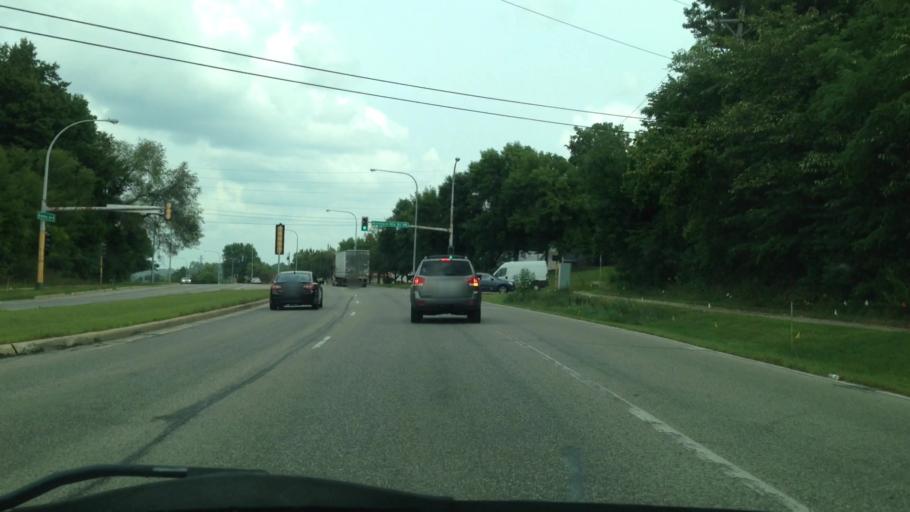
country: US
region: Minnesota
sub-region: Olmsted County
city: Rochester
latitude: 44.0469
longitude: -92.4567
